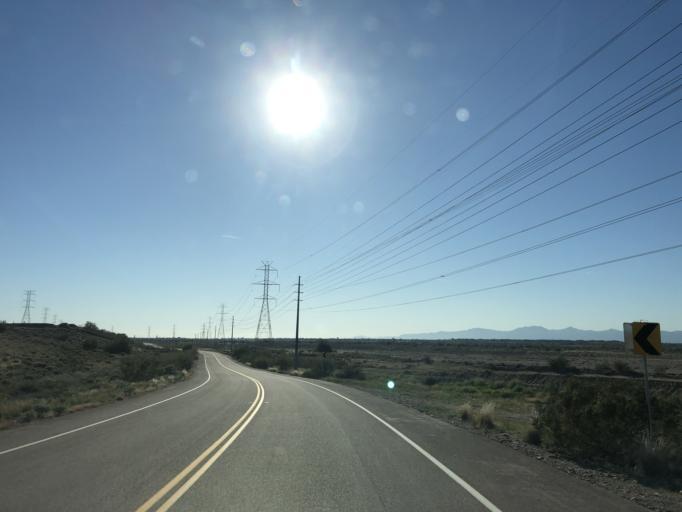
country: US
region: Arizona
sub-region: Maricopa County
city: Sun City West
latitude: 33.6953
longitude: -112.2925
